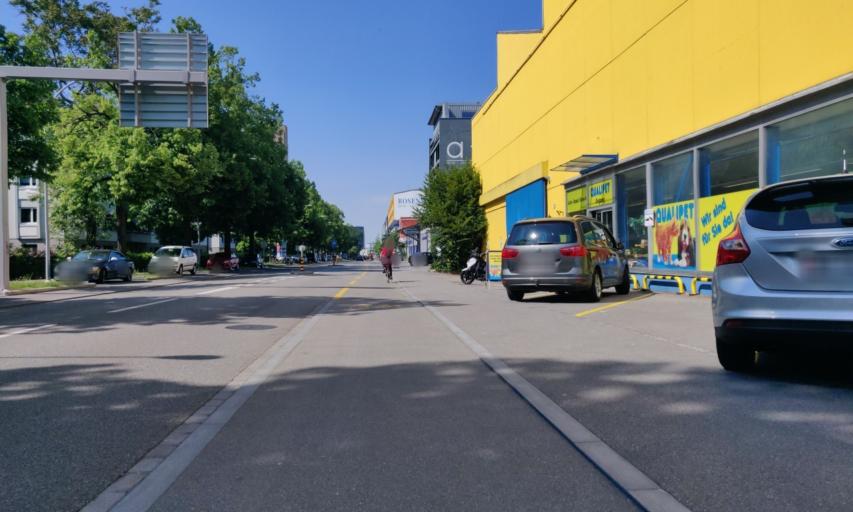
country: CH
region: Basel-Landschaft
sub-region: Bezirk Arlesheim
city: Munchenstein
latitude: 47.5312
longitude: 7.6055
